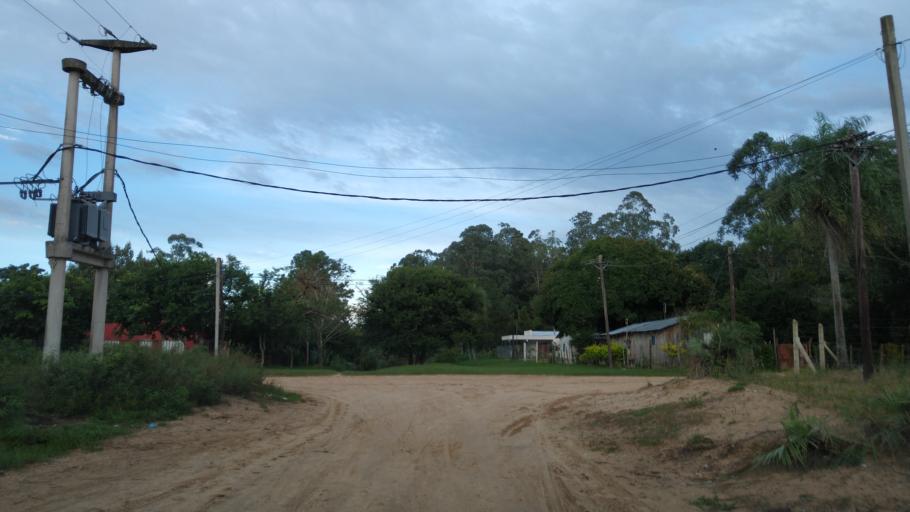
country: AR
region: Corrientes
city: Ituzaingo
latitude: -27.5951
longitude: -56.7091
